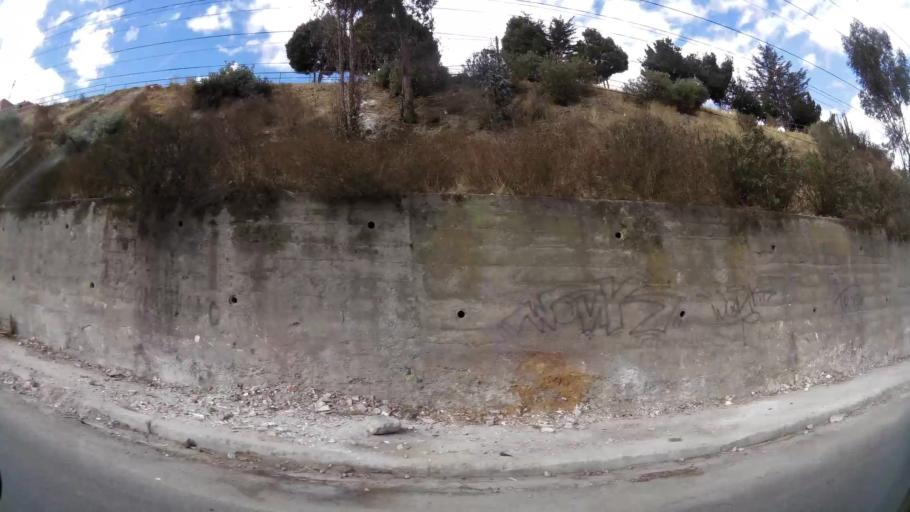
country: BO
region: La Paz
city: La Paz
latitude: -16.4728
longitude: -68.1516
